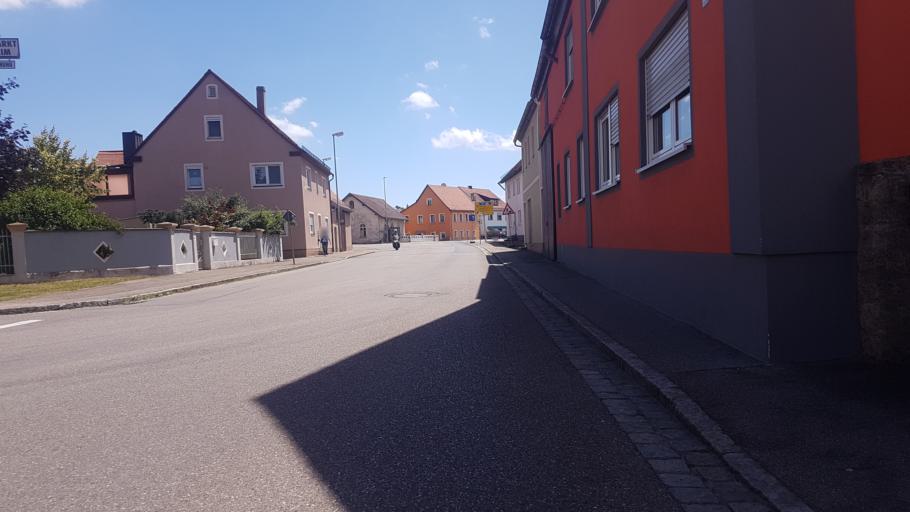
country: DE
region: Bavaria
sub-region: Regierungsbezirk Mittelfranken
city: Leutershausen
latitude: 49.2984
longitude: 10.4100
